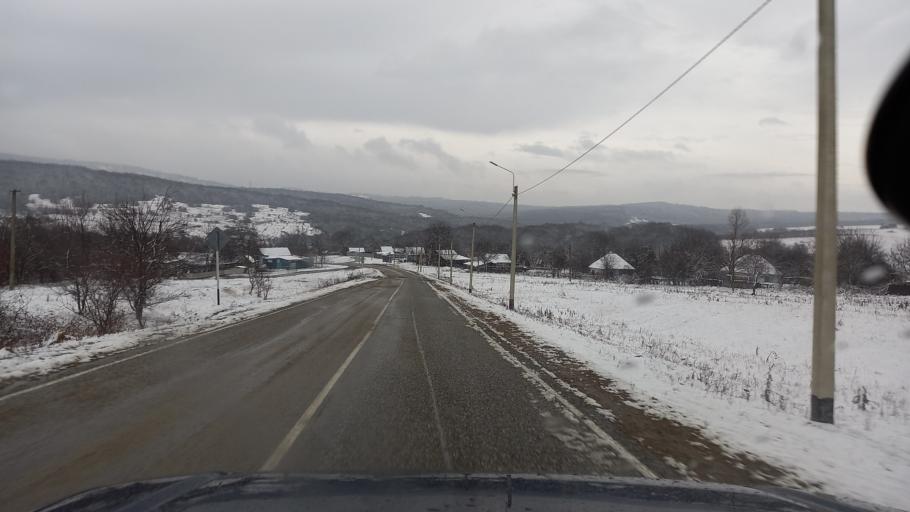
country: RU
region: Adygeya
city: Abadzekhskaya
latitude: 44.3482
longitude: 40.3225
